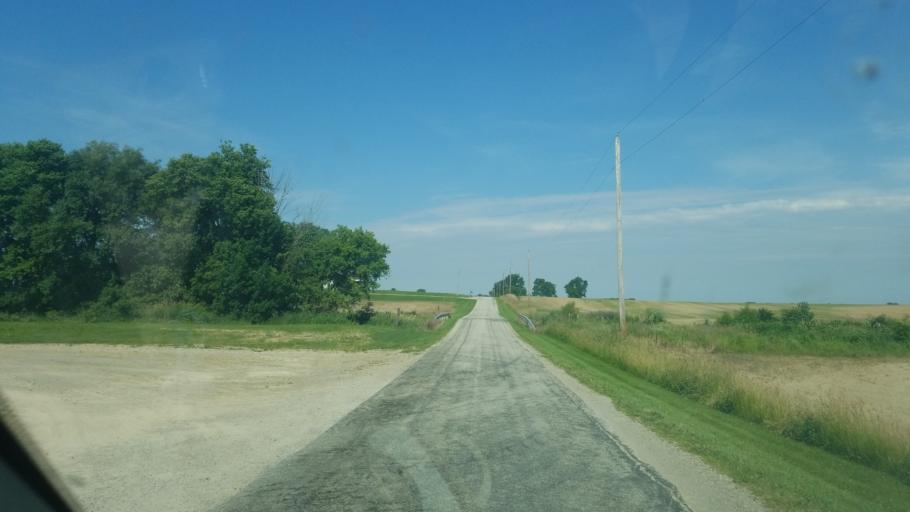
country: US
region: Ohio
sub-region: Wyandot County
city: Upper Sandusky
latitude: 40.9204
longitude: -83.2119
